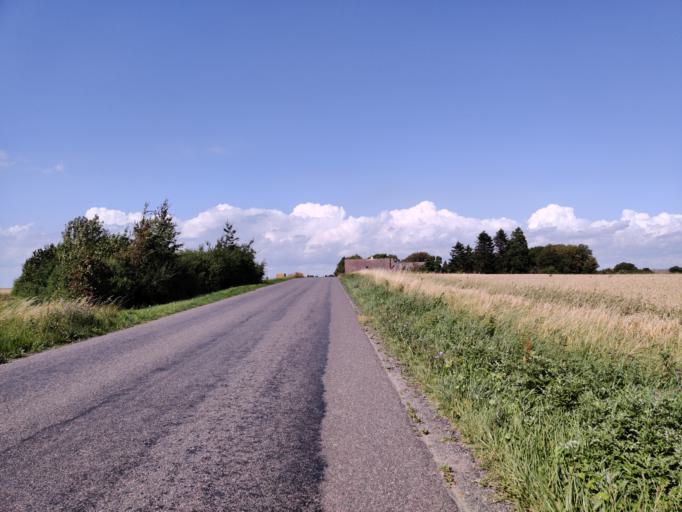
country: DK
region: Zealand
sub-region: Guldborgsund Kommune
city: Nykobing Falster
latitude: 54.6165
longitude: 11.9162
